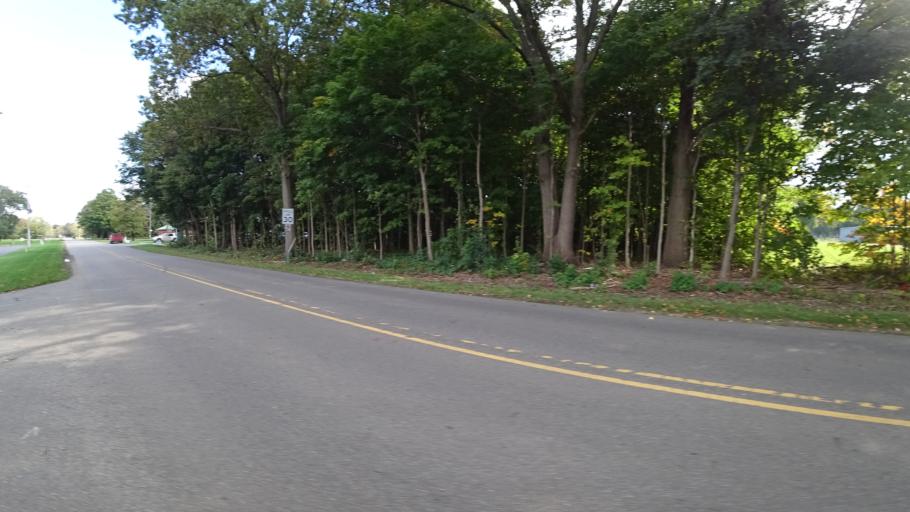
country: US
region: Michigan
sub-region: Saint Joseph County
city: Three Rivers
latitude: 41.9475
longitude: -85.6171
